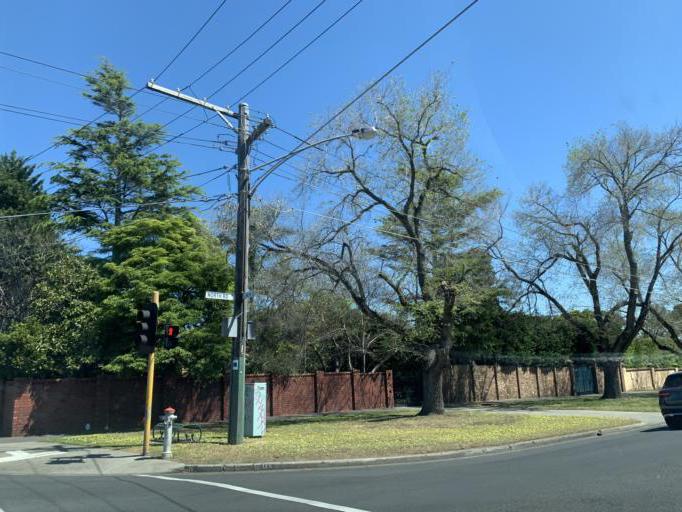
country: AU
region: Victoria
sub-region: Bayside
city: North Brighton
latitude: -37.8983
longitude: 144.9943
